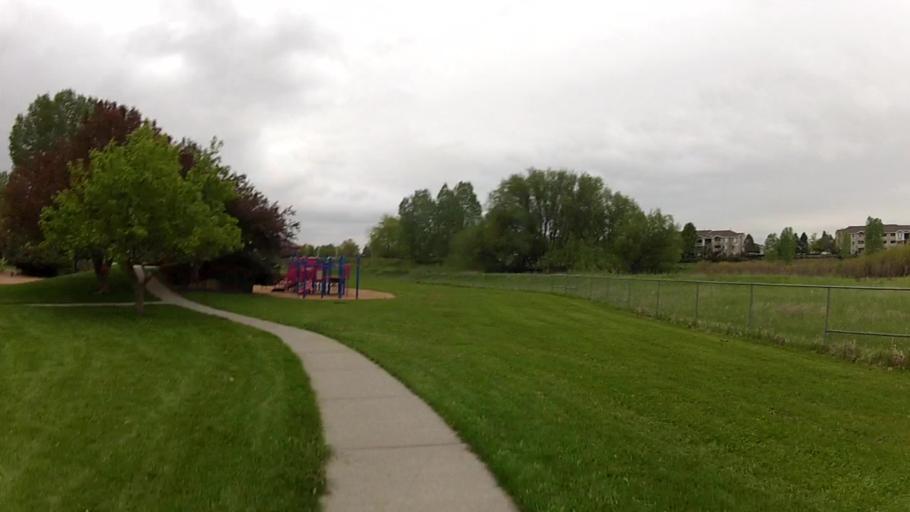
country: US
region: Colorado
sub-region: Larimer County
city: Fort Collins
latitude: 40.5561
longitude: -105.1018
